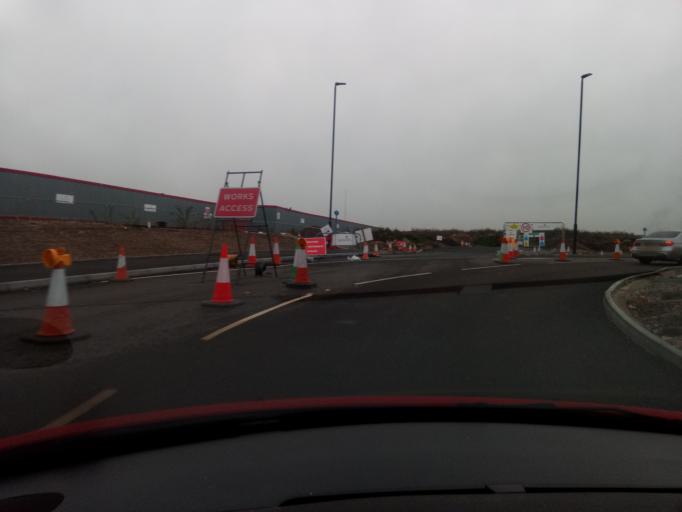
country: GB
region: England
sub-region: Derby
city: Derby
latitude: 52.9148
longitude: -1.4331
